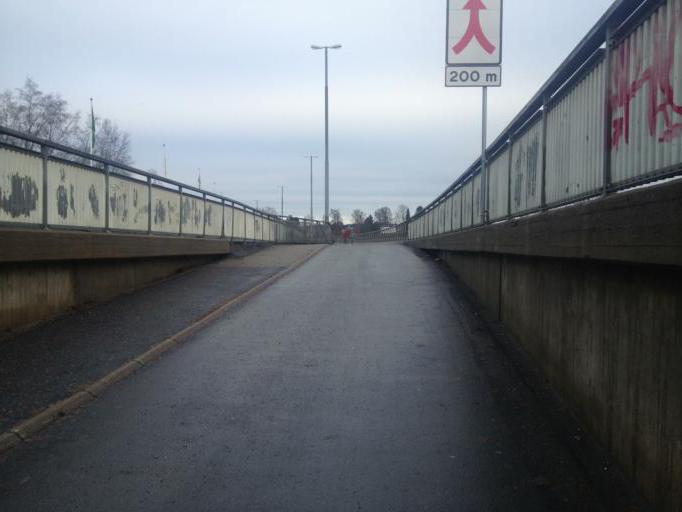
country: SE
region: Vaesterbotten
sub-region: Umea Kommun
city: Umea
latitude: 63.8192
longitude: 20.2650
